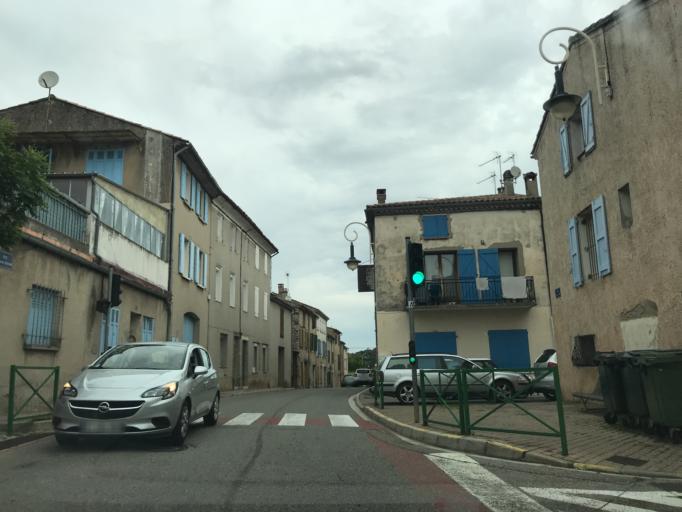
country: FR
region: Provence-Alpes-Cote d'Azur
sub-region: Departement du Var
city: Ginasservis
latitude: 43.6709
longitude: 5.8481
